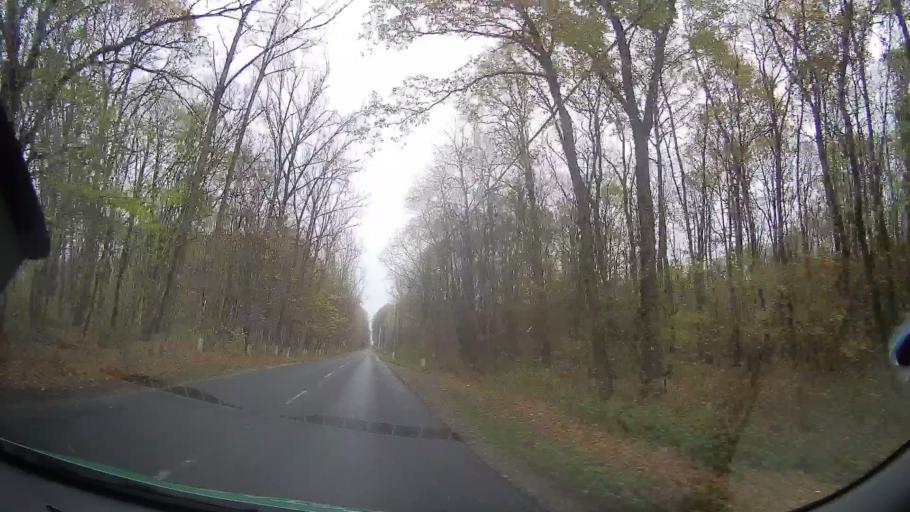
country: RO
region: Ilfov
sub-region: Comuna Snagov
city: Snagov
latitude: 44.7160
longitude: 26.1975
